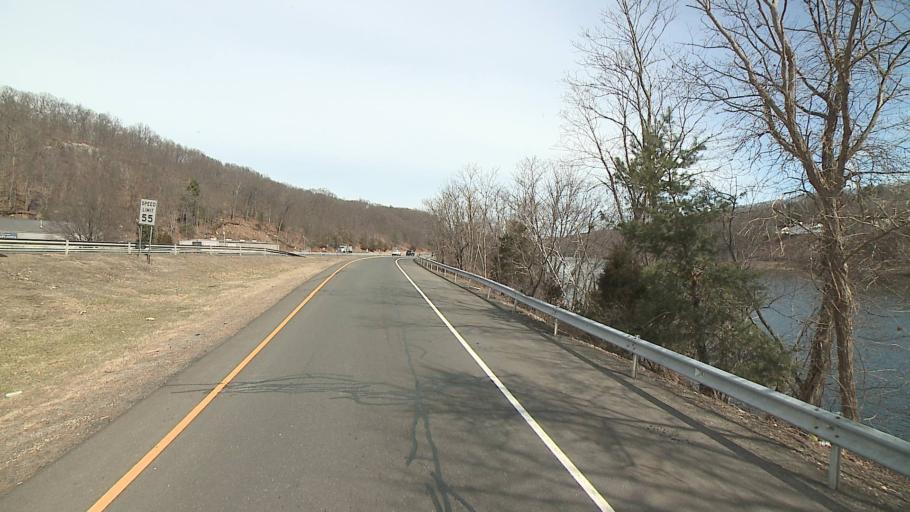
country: US
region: Connecticut
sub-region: New Haven County
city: Ansonia
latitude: 41.3695
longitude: -73.0860
